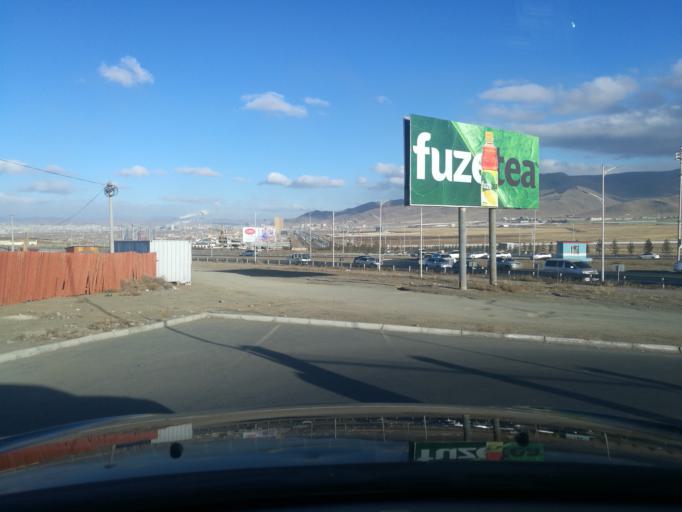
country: MN
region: Ulaanbaatar
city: Ulaanbaatar
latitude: 47.8581
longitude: 106.7856
